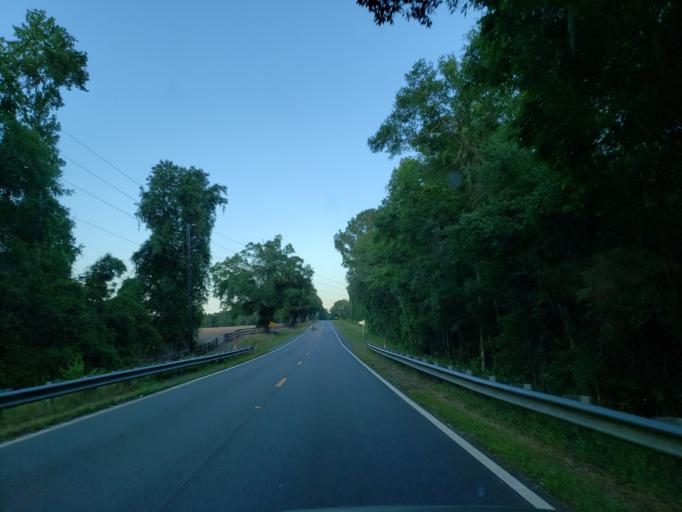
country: US
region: Georgia
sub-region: Echols County
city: Statenville
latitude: 30.5813
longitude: -83.2039
